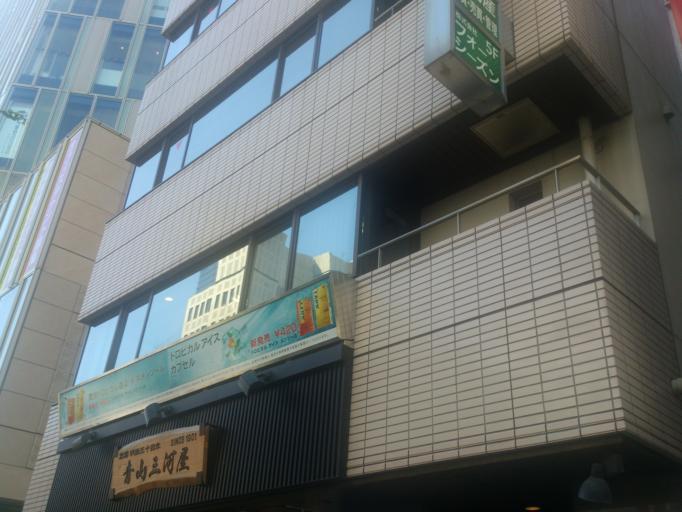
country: JP
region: Tokyo
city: Tokyo
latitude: 35.6640
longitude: 139.7116
